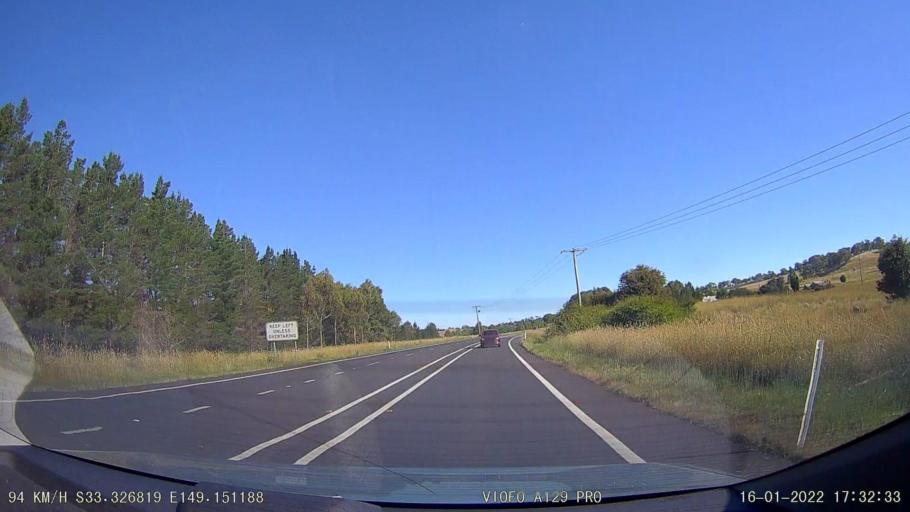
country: AU
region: New South Wales
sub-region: Orange Municipality
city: Orange
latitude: -33.3267
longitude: 149.1511
